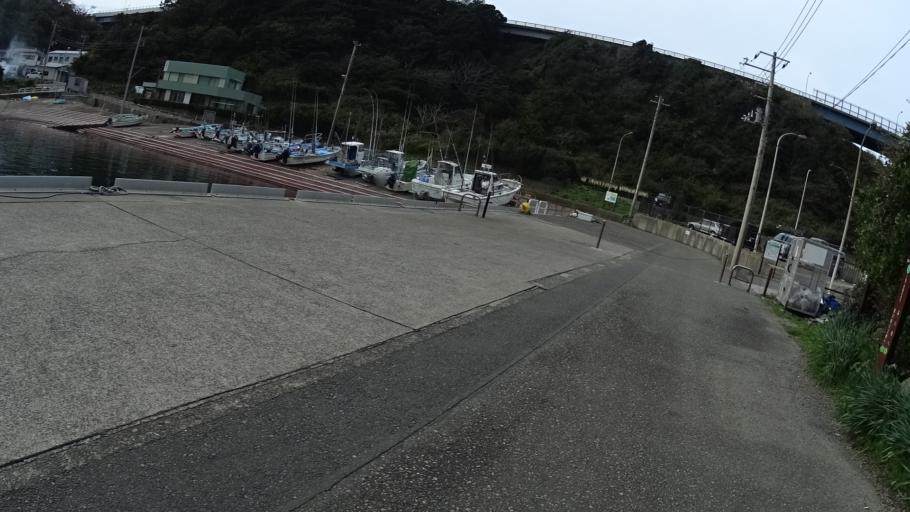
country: JP
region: Kanagawa
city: Miura
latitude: 35.1419
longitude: 139.6380
